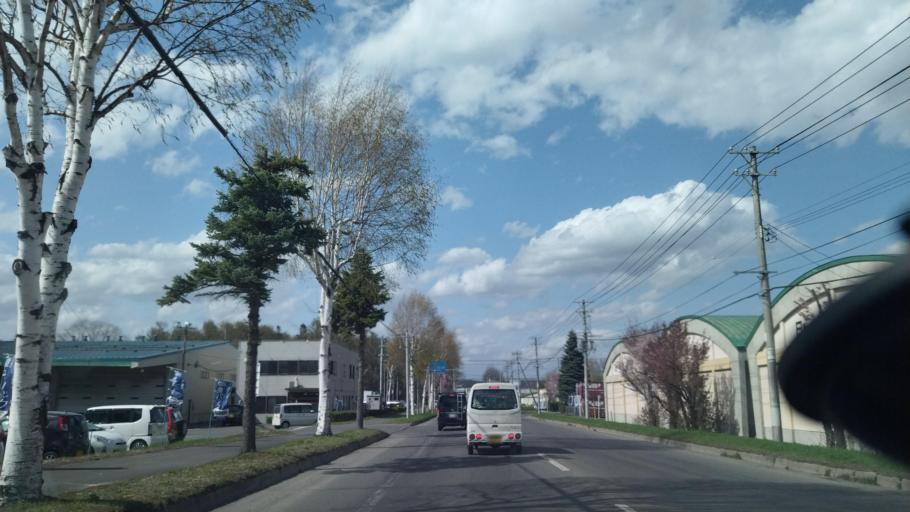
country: JP
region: Hokkaido
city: Obihiro
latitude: 42.9260
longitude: 143.1434
